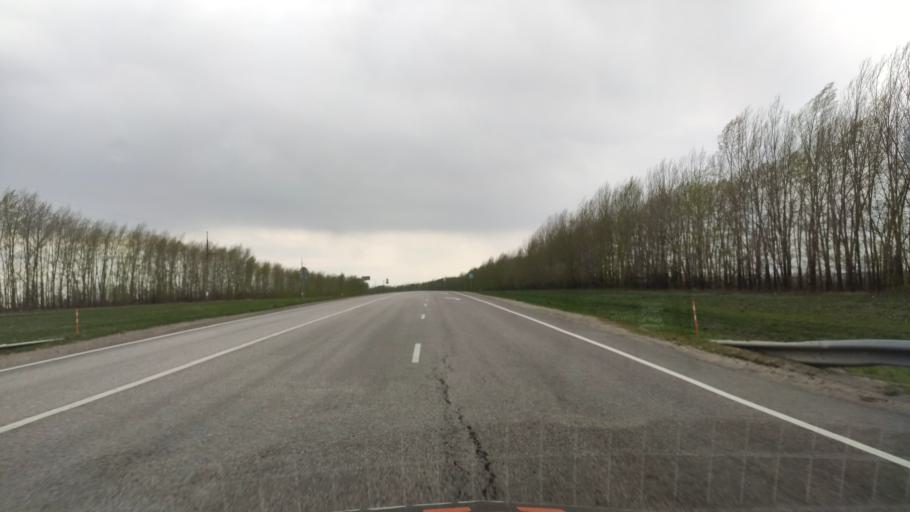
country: RU
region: Voronezj
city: Nizhnedevitsk
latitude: 51.5655
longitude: 38.4563
